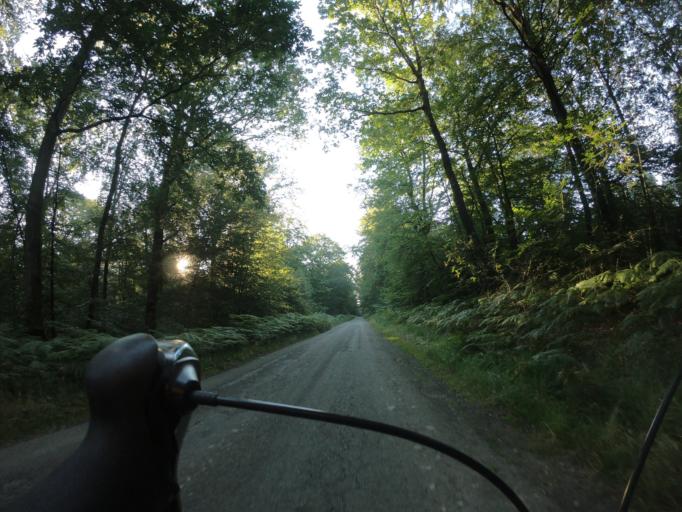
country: FR
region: Lower Normandy
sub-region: Departement de l'Orne
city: Magny-le-Desert
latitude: 48.5406
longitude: -0.3358
